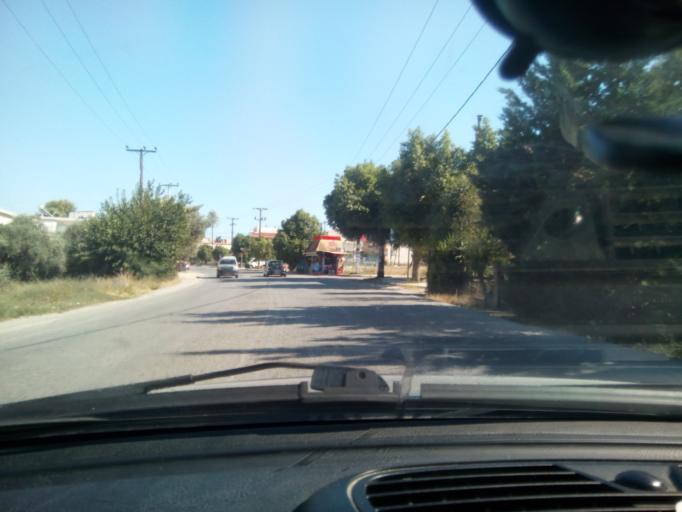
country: GR
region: Central Greece
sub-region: Nomos Evvoias
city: Vasilikon
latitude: 38.4237
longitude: 23.6752
